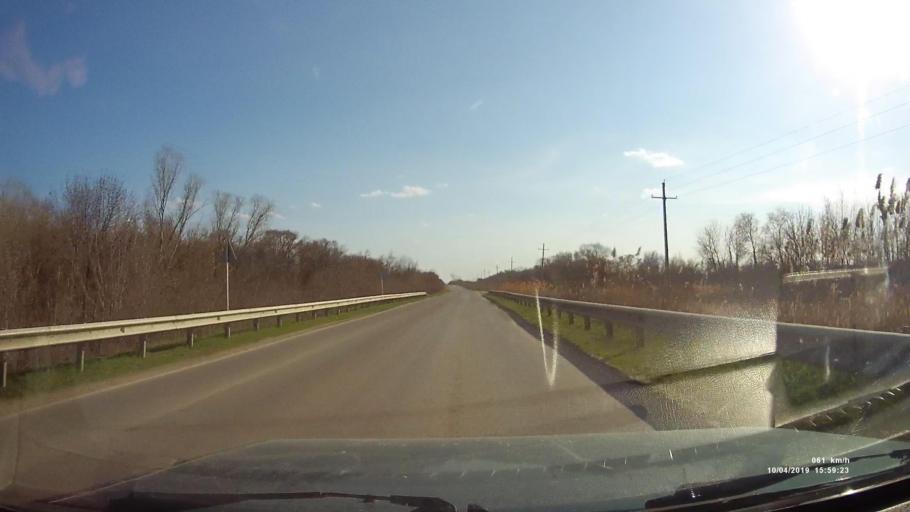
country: RU
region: Rostov
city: Masalovka
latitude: 48.3948
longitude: 40.2685
